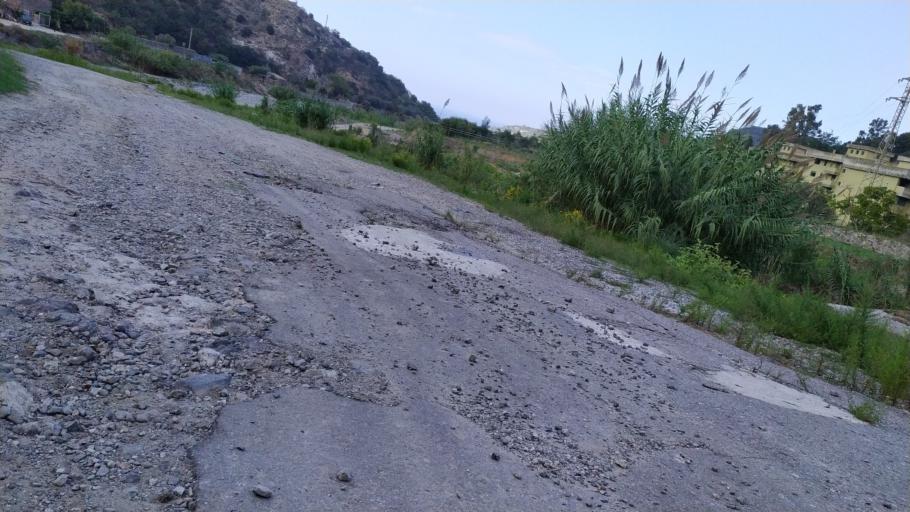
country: IT
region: Sicily
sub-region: Messina
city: Saponara
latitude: 38.1951
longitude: 15.4300
